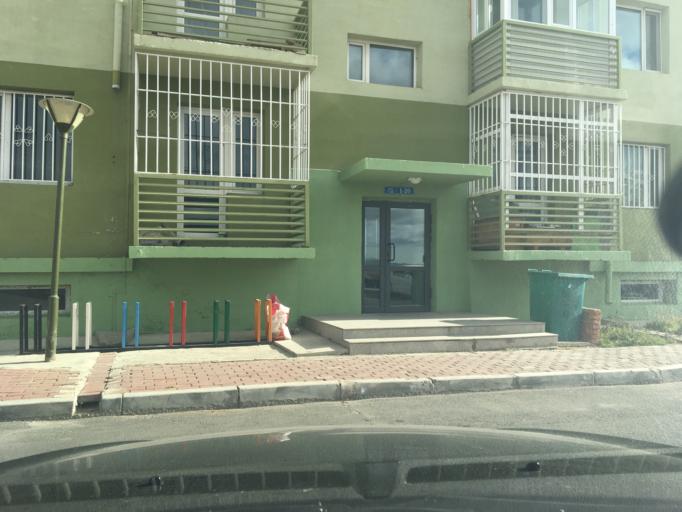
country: MN
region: Ulaanbaatar
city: Ulaanbaatar
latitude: 47.8794
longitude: 106.8478
